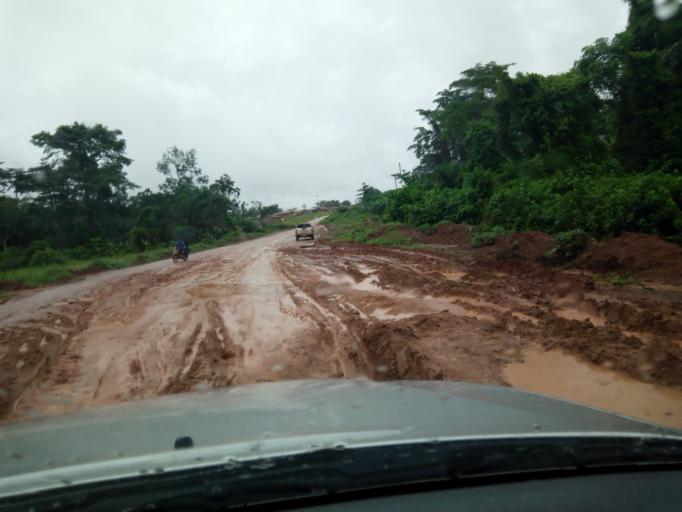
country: LR
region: Nimba
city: Sanniquellie
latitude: 7.0345
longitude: -8.8506
